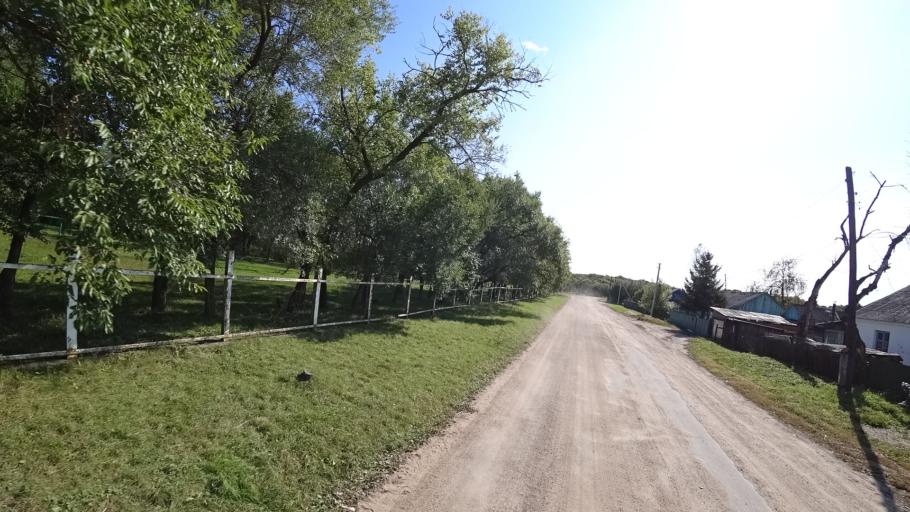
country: RU
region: Amur
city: Arkhara
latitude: 49.4023
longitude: 130.1380
